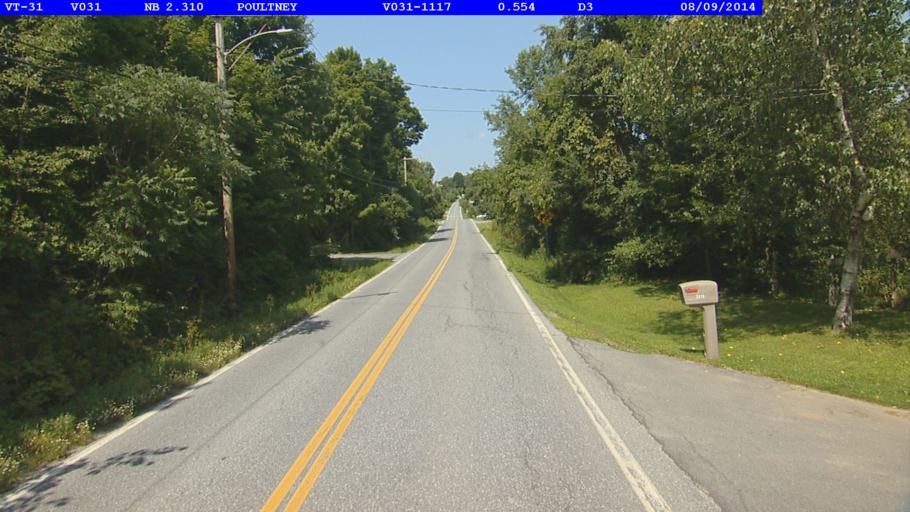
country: US
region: Vermont
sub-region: Rutland County
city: Poultney
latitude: 43.4700
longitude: -73.2431
